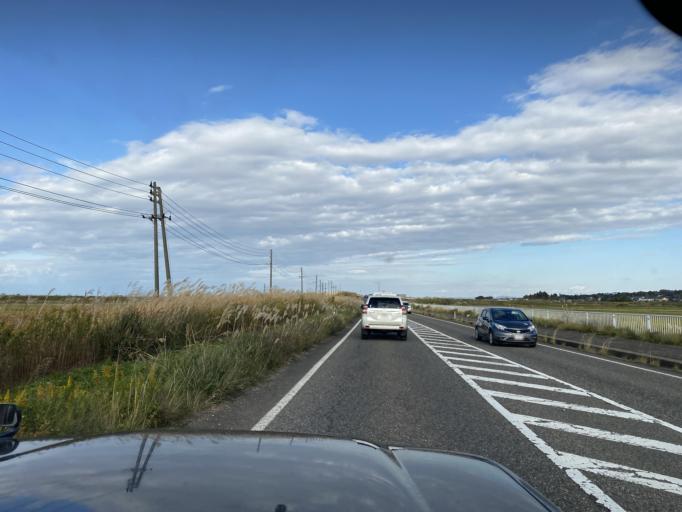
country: JP
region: Niigata
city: Niitsu-honcho
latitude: 37.7743
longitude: 139.1051
